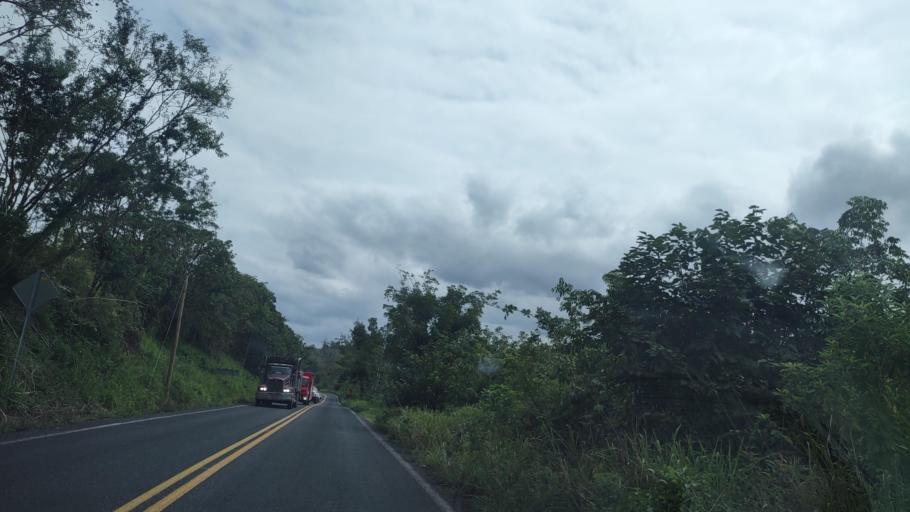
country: MX
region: Veracruz
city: Papantla de Olarte
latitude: 20.4633
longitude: -97.2709
